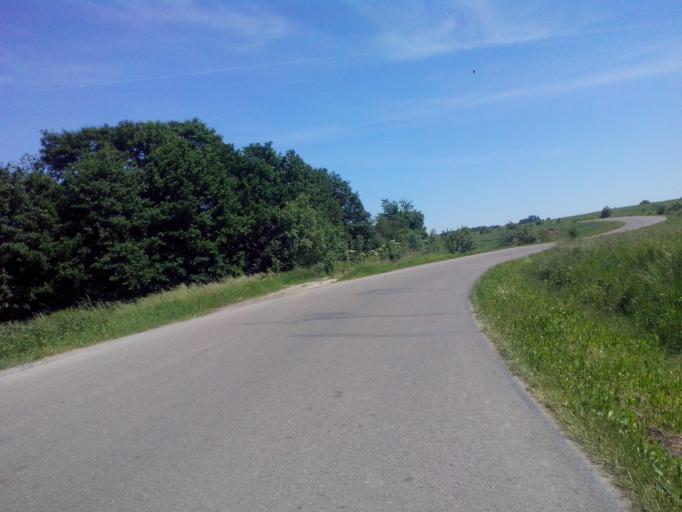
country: PL
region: Subcarpathian Voivodeship
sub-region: Powiat strzyzowski
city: Wisniowa
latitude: 49.8572
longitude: 21.6910
